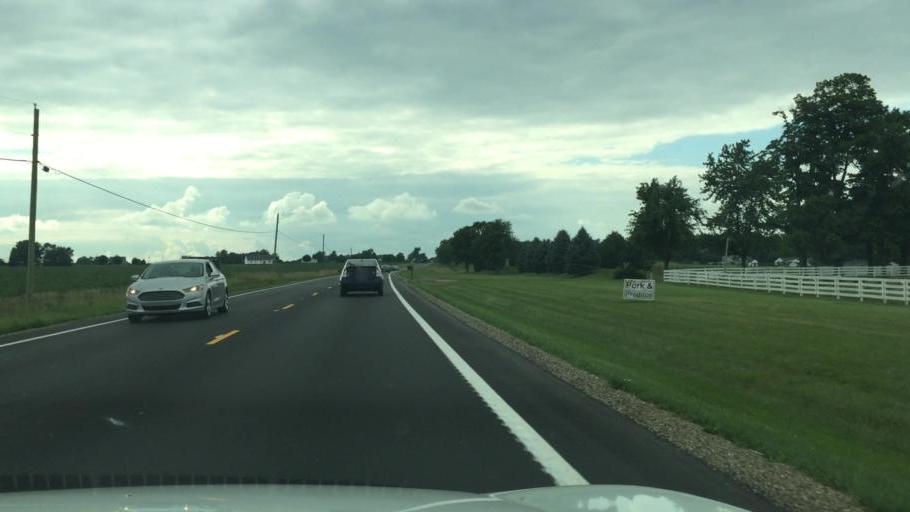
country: US
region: Ohio
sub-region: Champaign County
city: Urbana
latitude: 40.0877
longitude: -83.6857
